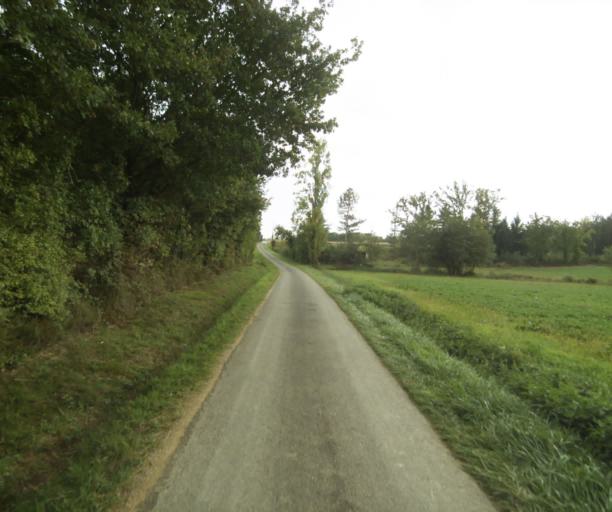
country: FR
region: Midi-Pyrenees
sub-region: Departement du Gers
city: Gondrin
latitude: 43.8596
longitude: 0.2209
